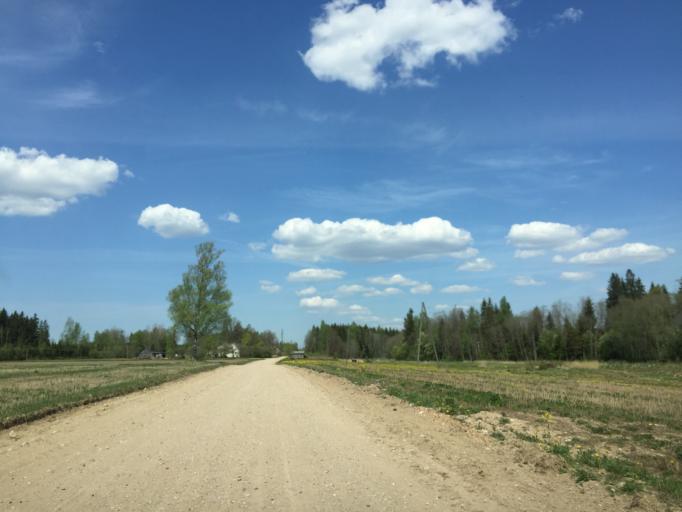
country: LV
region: Limbazu Rajons
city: Limbazi
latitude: 57.3625
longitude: 24.6386
